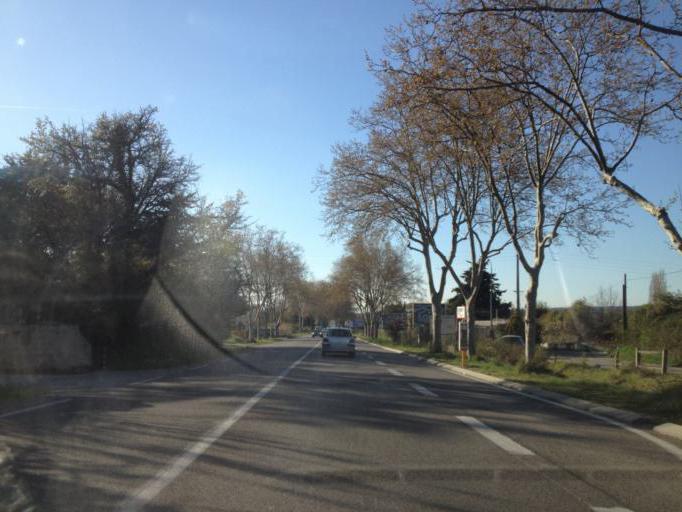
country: FR
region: Provence-Alpes-Cote d'Azur
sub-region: Departement des Bouches-du-Rhone
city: Eguilles
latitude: 43.5654
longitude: 5.4038
